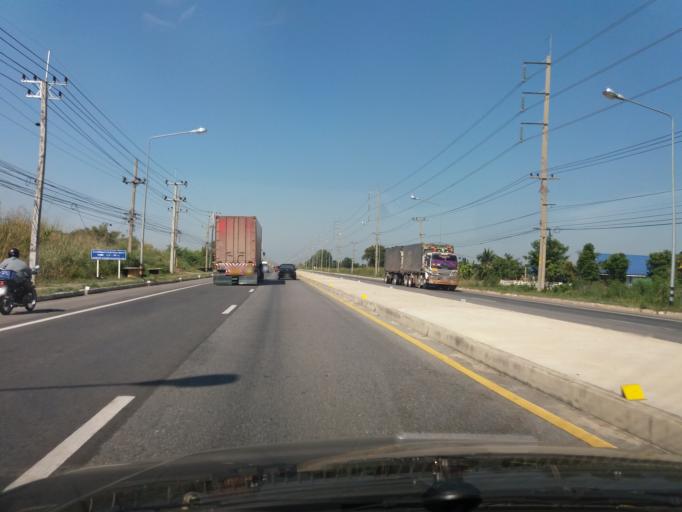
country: TH
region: Chai Nat
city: Manorom
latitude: 15.2884
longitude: 100.0977
